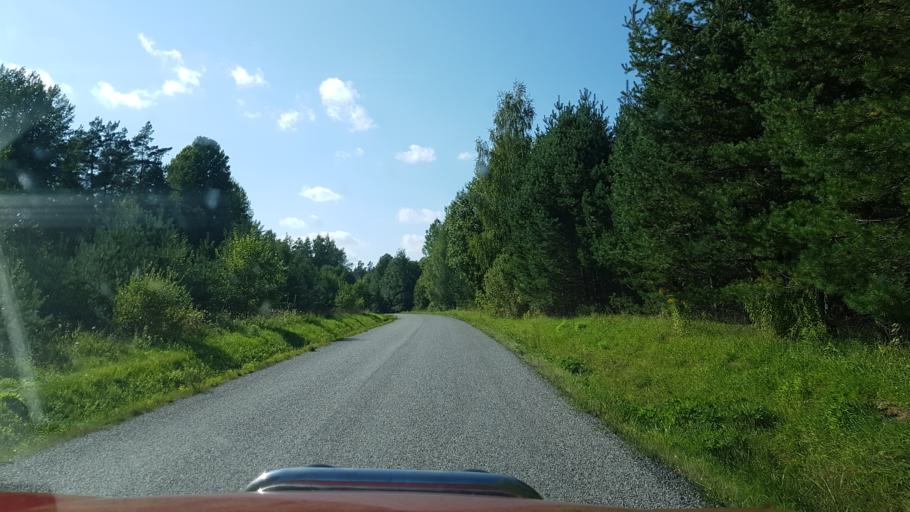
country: RU
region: Pskov
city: Pechory
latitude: 57.9503
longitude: 27.5984
